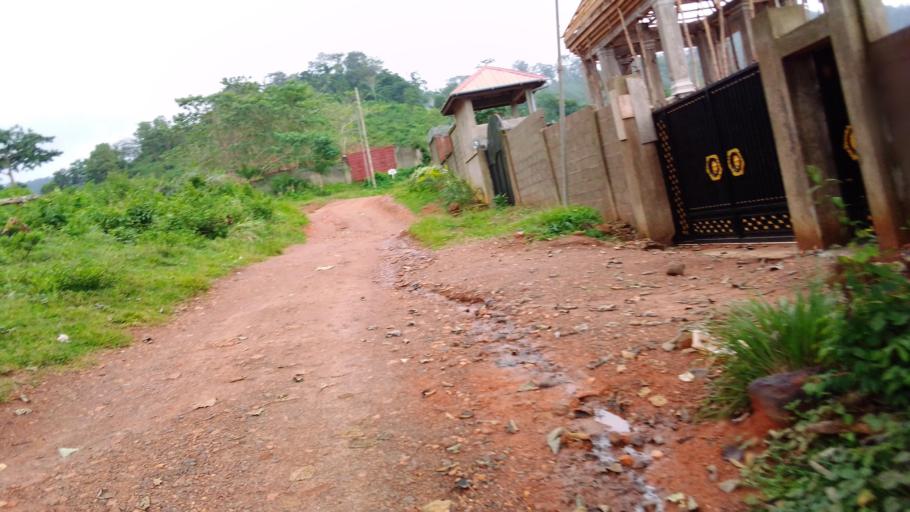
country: SL
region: Eastern Province
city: Kenema
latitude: 7.8908
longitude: -11.1950
